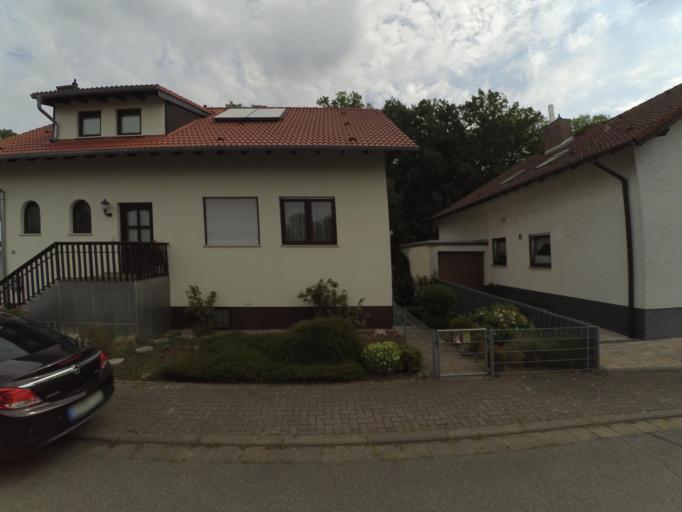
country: DE
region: Hesse
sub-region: Regierungsbezirk Darmstadt
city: Alsbach-Hahnlein
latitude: 49.7089
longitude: 8.5757
